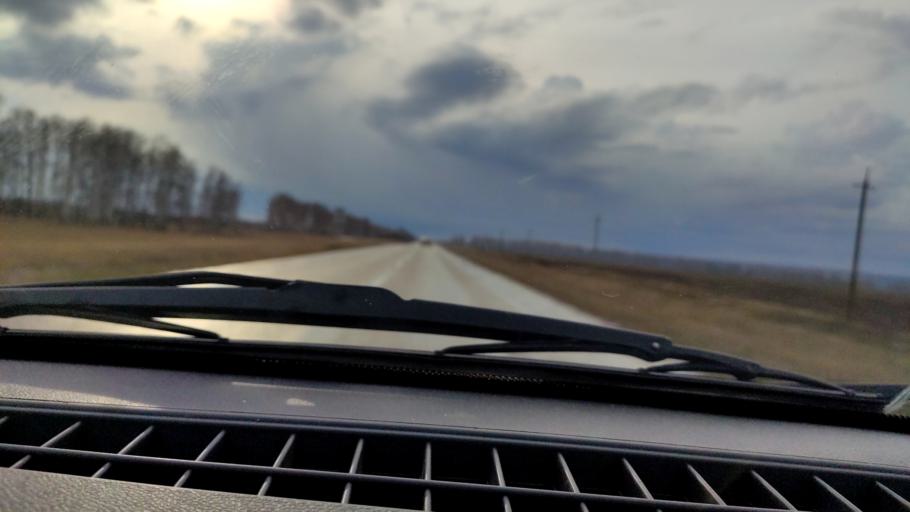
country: RU
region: Bashkortostan
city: Alekseyevka
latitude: 55.1050
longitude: 55.0142
